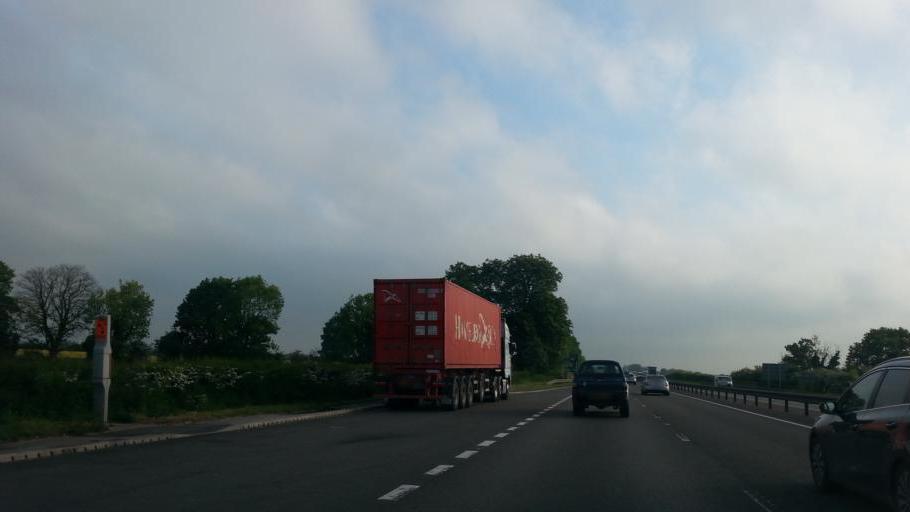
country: GB
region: England
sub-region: Nottinghamshire
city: South Collingham
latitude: 53.1360
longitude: -0.8081
